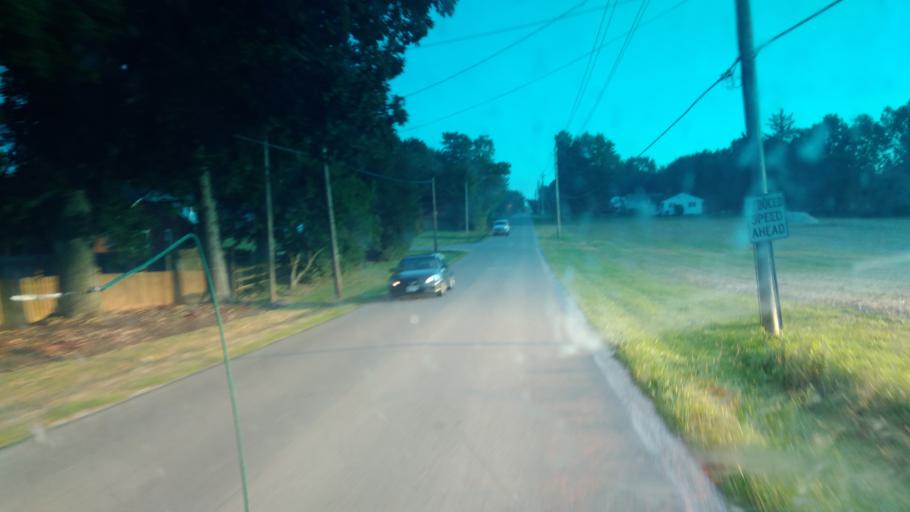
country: US
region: Ohio
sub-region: Crawford County
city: Galion
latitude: 40.7426
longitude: -82.8200
